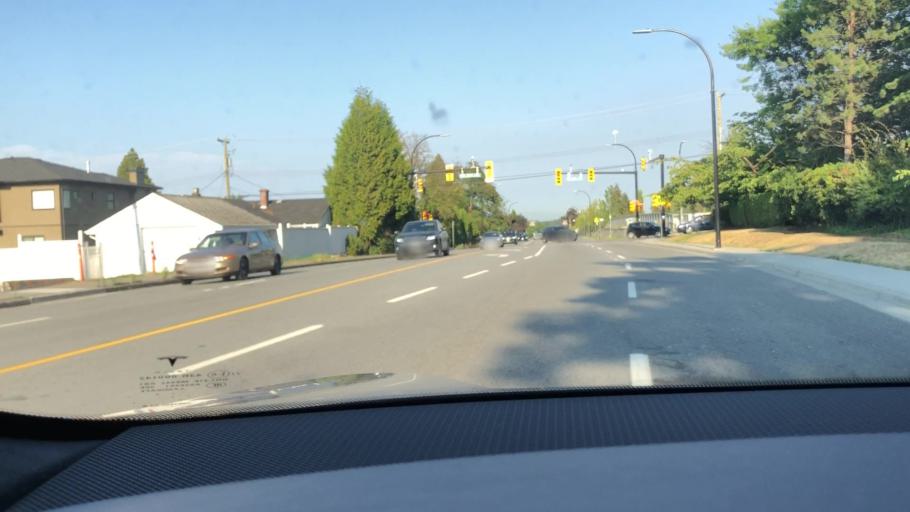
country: CA
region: British Columbia
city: Burnaby
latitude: 49.2299
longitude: -122.9953
